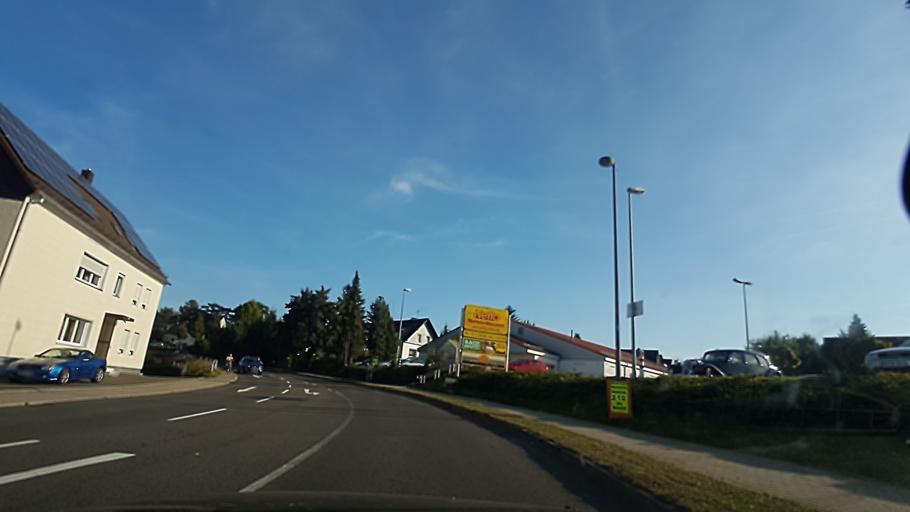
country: DE
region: North Rhine-Westphalia
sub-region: Regierungsbezirk Koln
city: Marienheide
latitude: 51.0807
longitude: 7.5356
